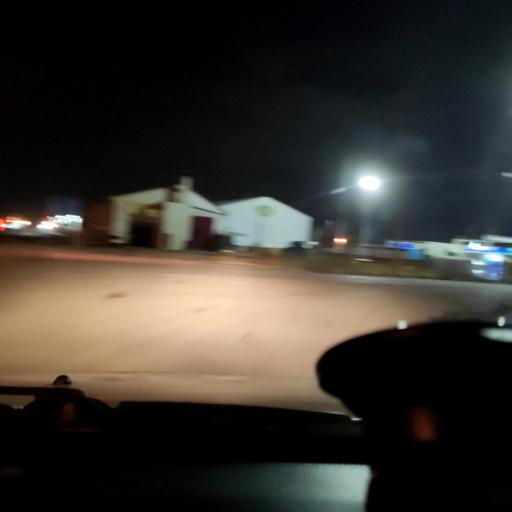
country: RU
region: Perm
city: Froly
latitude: 57.9569
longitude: 56.2883
